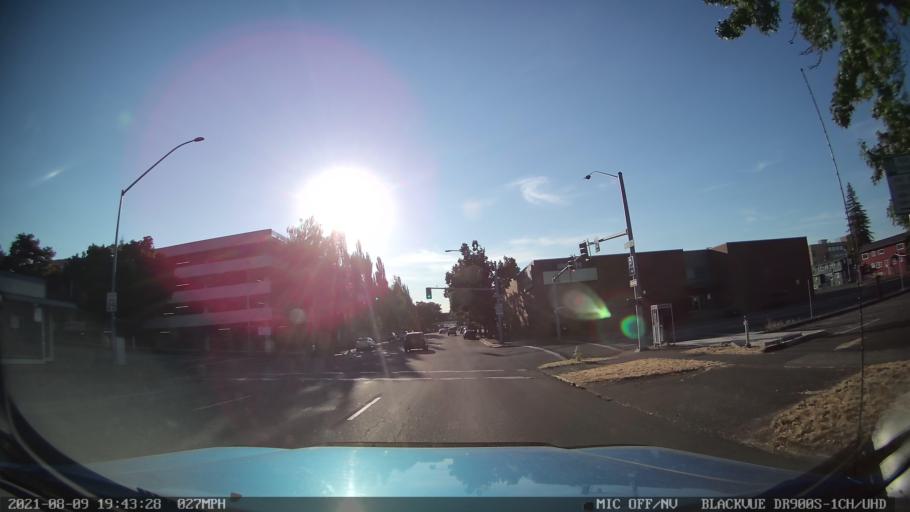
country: US
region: Oregon
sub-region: Marion County
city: Salem
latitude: 44.9434
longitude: -123.0328
